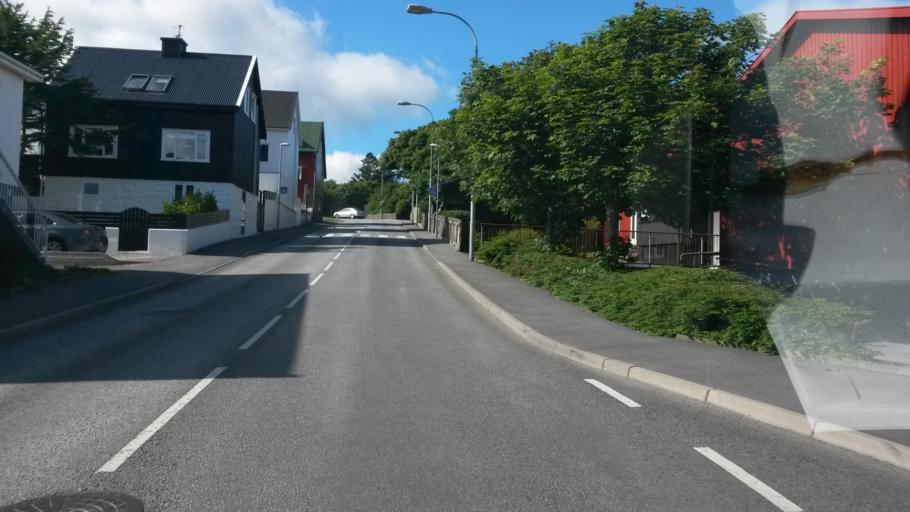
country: FO
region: Streymoy
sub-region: Torshavn
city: Torshavn
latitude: 62.0105
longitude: -6.7671
